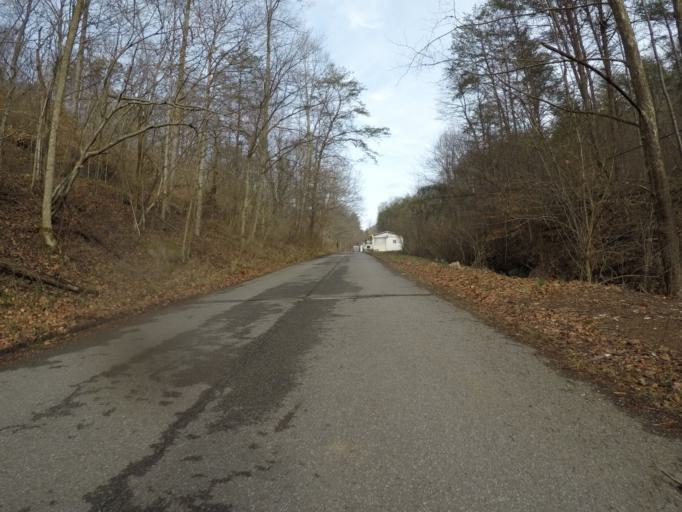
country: US
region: West Virginia
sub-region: Wayne County
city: Lavalette
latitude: 38.3347
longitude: -82.3771
